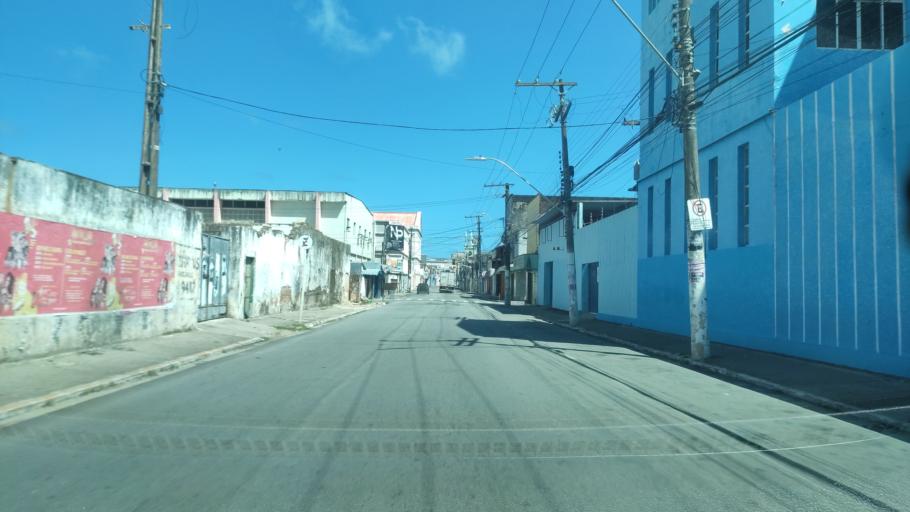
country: BR
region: Alagoas
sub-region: Maceio
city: Maceio
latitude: -9.6633
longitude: -35.7423
